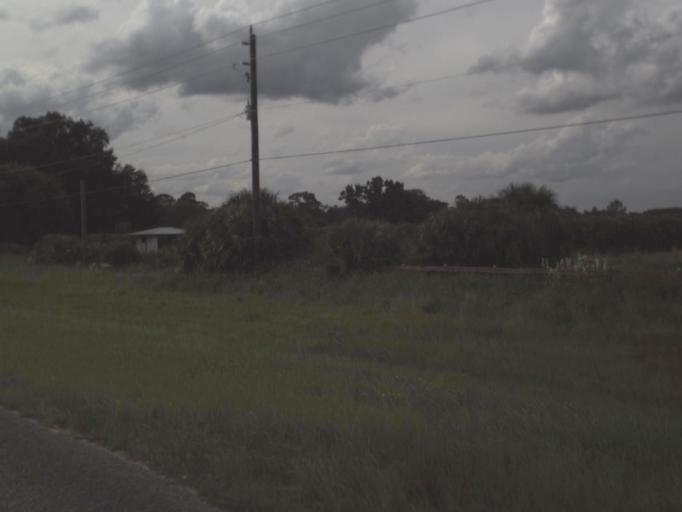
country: US
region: Florida
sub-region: Lee County
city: Alva
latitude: 26.7097
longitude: -81.5393
